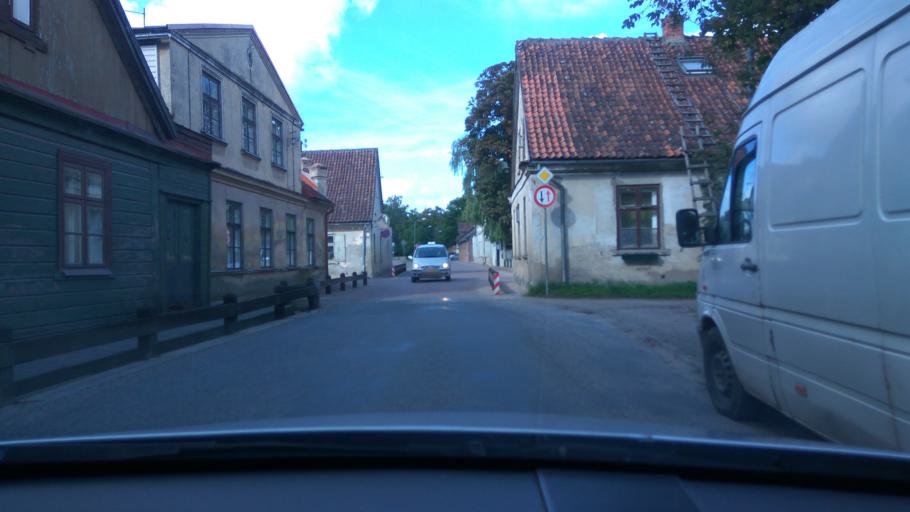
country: LV
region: Kuldigas Rajons
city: Kuldiga
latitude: 56.9671
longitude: 21.9680
